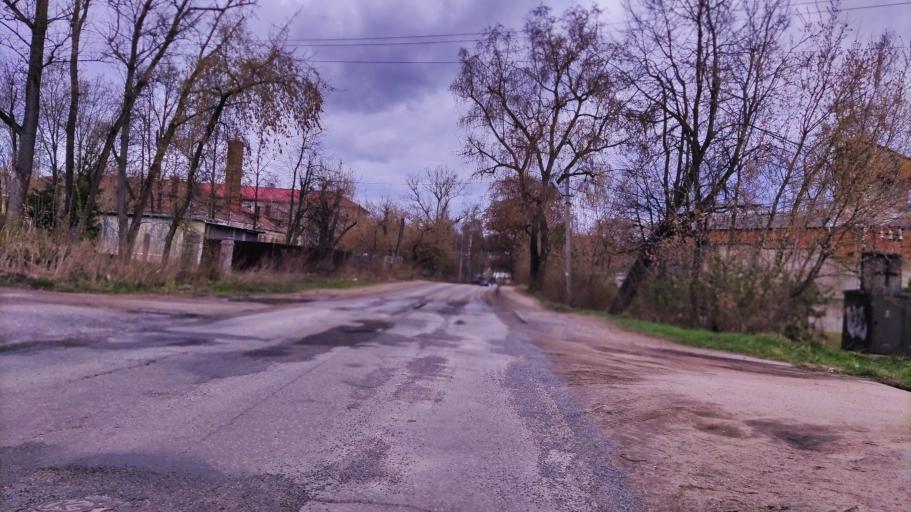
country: RU
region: Tverskaya
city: Rzhev
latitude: 56.2564
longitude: 34.3360
